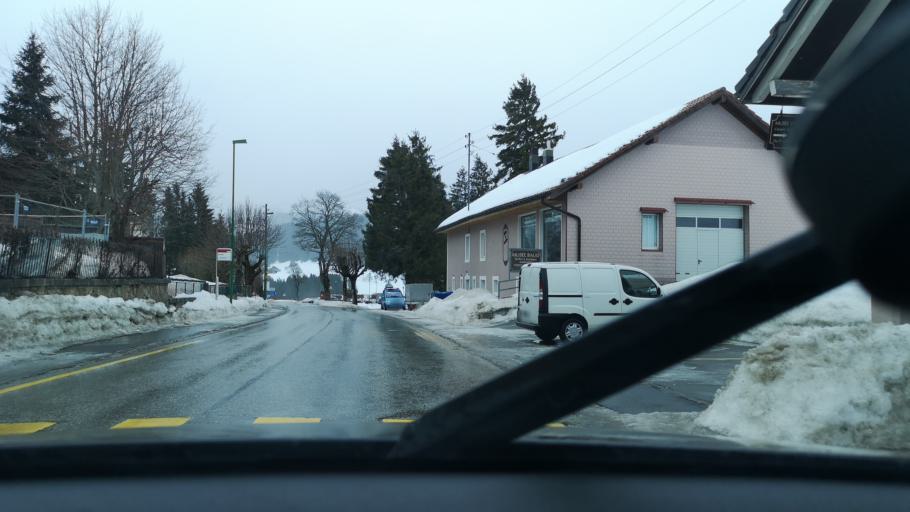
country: CH
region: Vaud
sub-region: Jura-Nord vaudois District
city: Sainte-Croix
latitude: 46.8197
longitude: 6.4705
